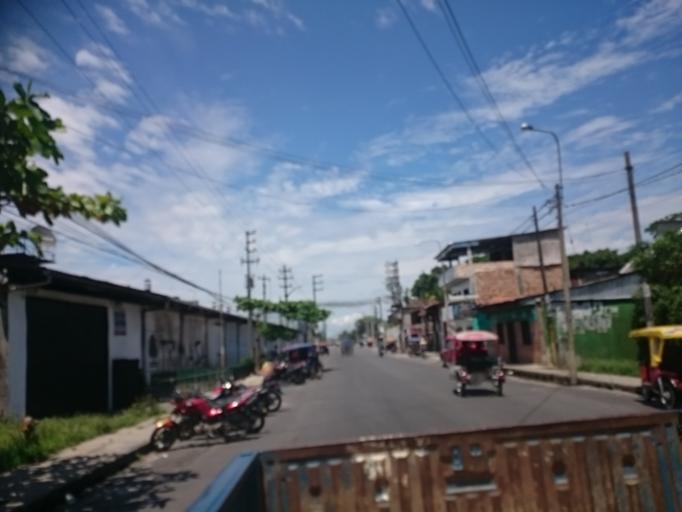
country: PE
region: Loreto
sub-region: Provincia de Maynas
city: Iquitos
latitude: -3.7158
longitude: -73.2450
